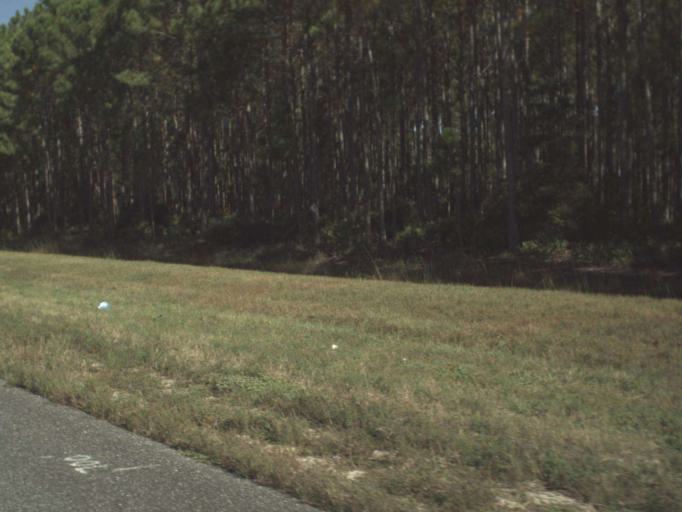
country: US
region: Florida
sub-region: Bay County
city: Laguna Beach
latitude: 30.2921
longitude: -86.0208
